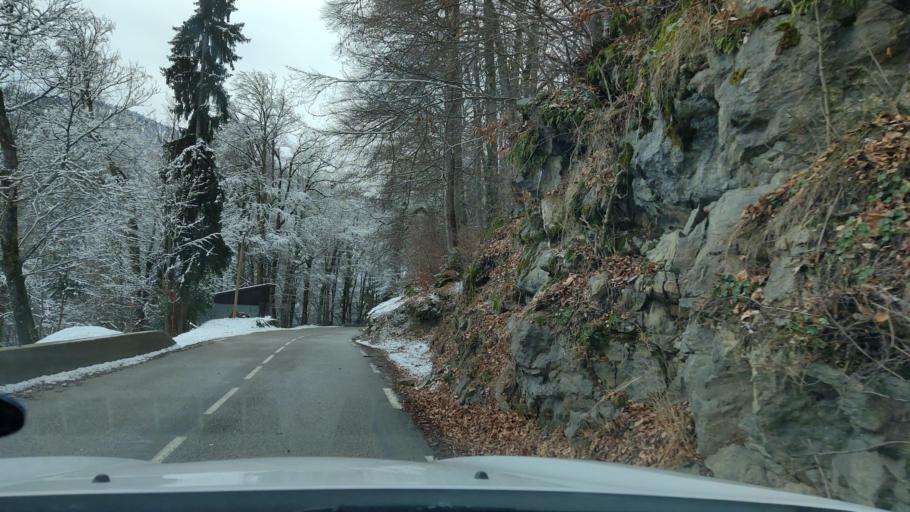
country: FR
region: Rhone-Alpes
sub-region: Departement de la Savoie
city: Ugine
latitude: 45.7660
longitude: 6.4695
